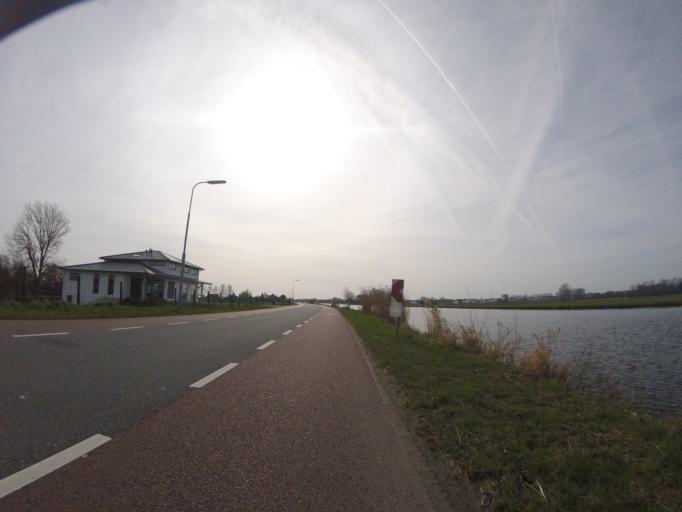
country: NL
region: North Holland
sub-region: Gemeente Bloemendaal
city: Bennebroek
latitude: 52.3060
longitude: 4.6052
